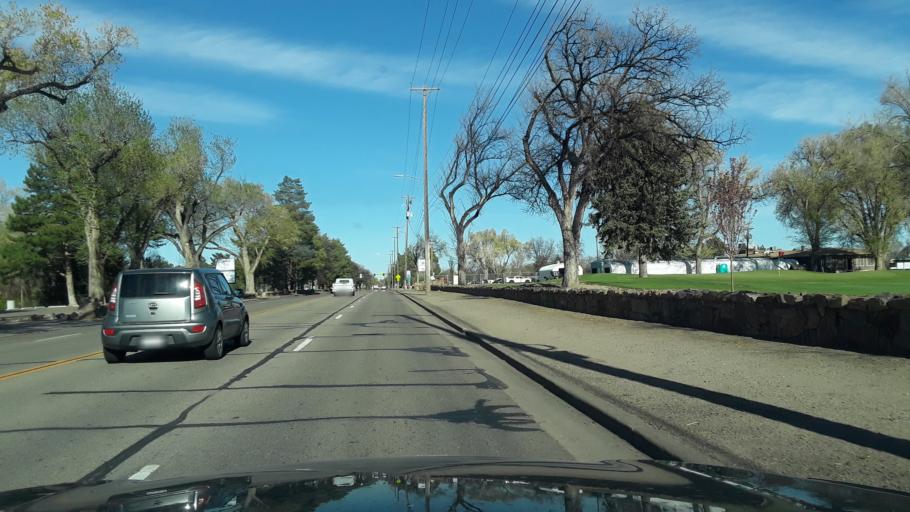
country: US
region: Colorado
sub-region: Pueblo County
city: Pueblo
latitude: 38.2584
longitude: -104.6572
